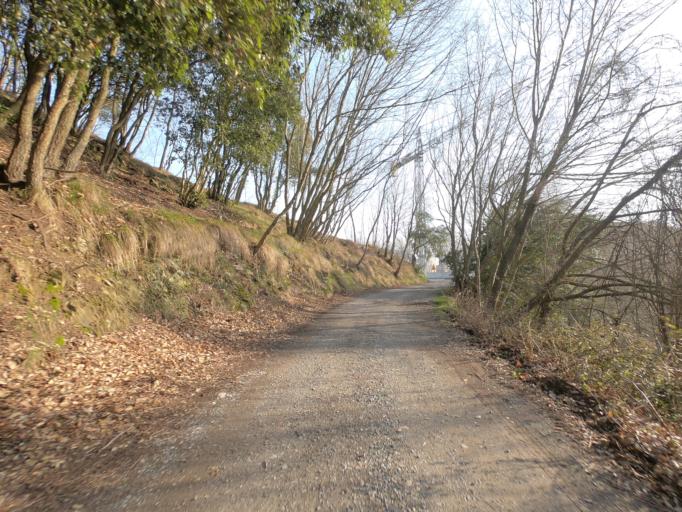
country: IT
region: Liguria
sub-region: Provincia di Savona
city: Balestrino
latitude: 44.1109
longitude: 8.1619
